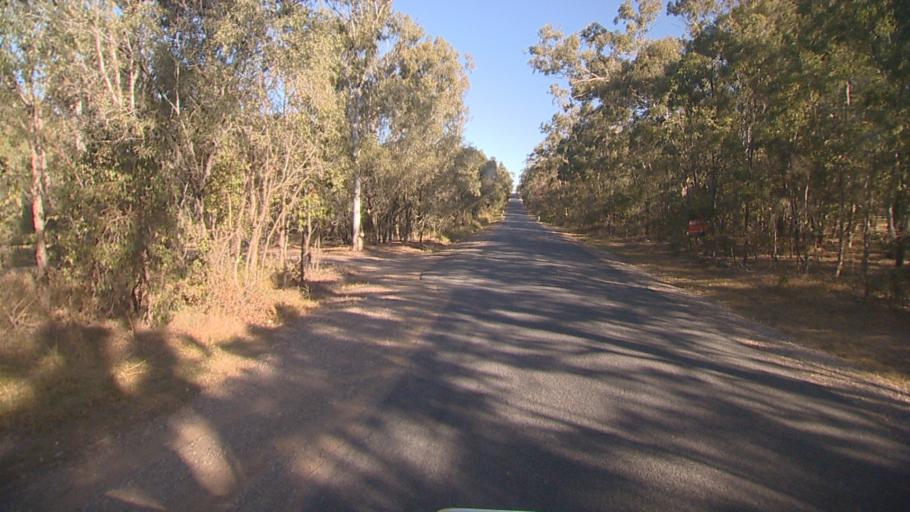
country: AU
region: Queensland
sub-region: Logan
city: North Maclean
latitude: -27.7933
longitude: 153.0268
